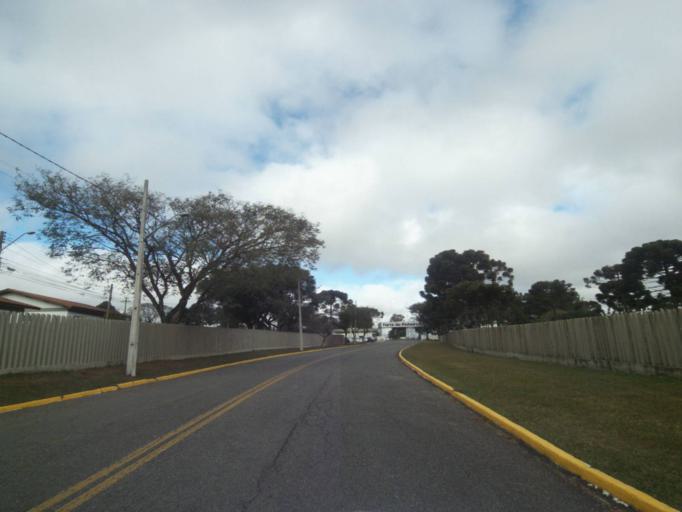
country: BR
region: Parana
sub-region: Sao Jose Dos Pinhais
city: Sao Jose dos Pinhais
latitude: -25.5268
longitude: -49.3024
